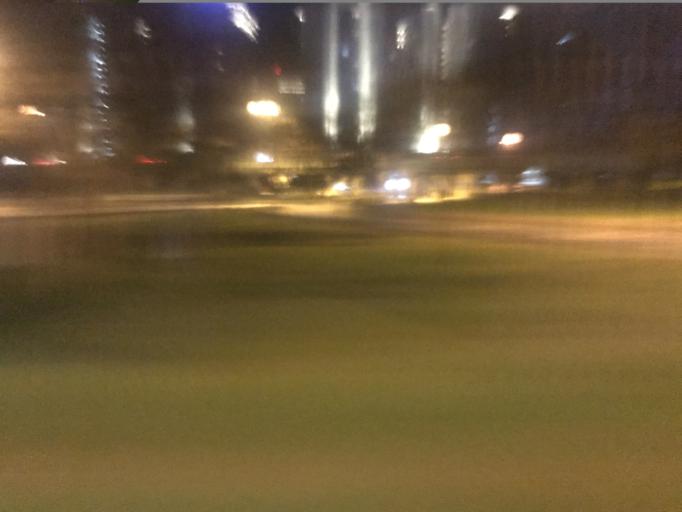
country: TR
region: Istanbul
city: Bahcelievler
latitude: 40.9769
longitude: 28.8518
